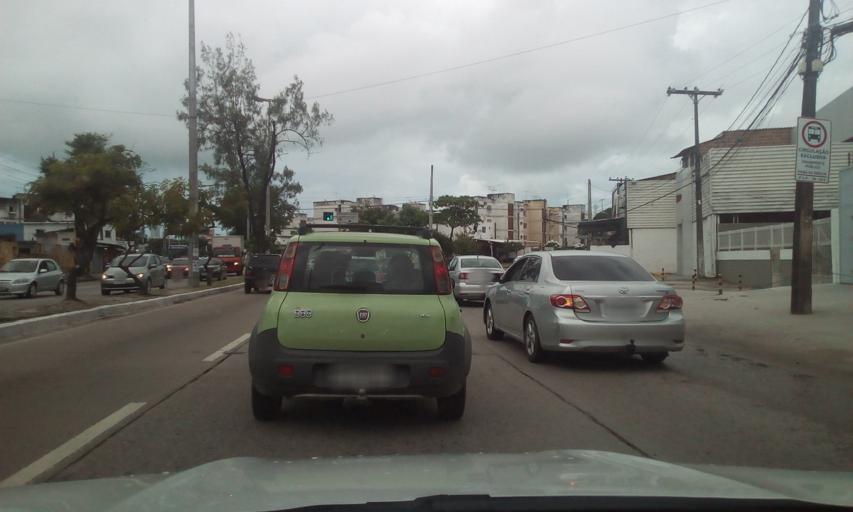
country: BR
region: Pernambuco
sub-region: Recife
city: Recife
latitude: -8.1189
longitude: -34.9216
